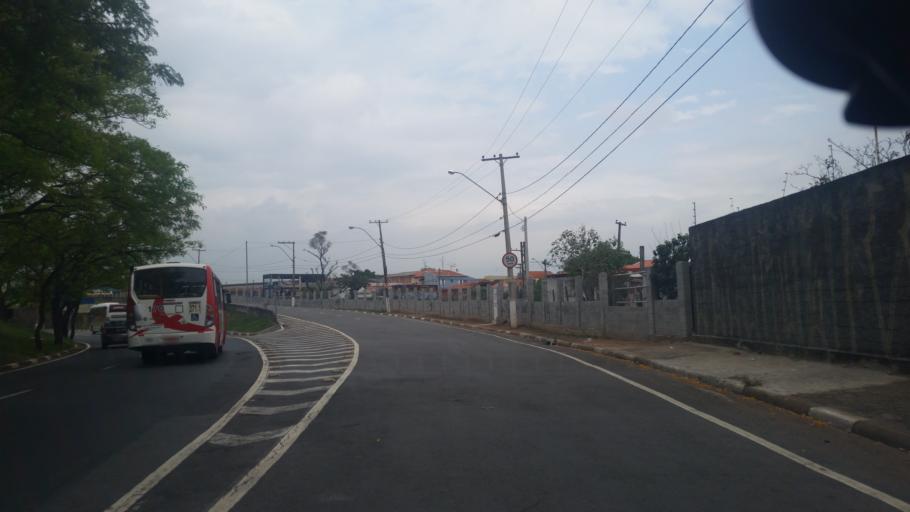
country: BR
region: Sao Paulo
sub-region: Campinas
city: Campinas
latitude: -22.9052
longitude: -47.0767
